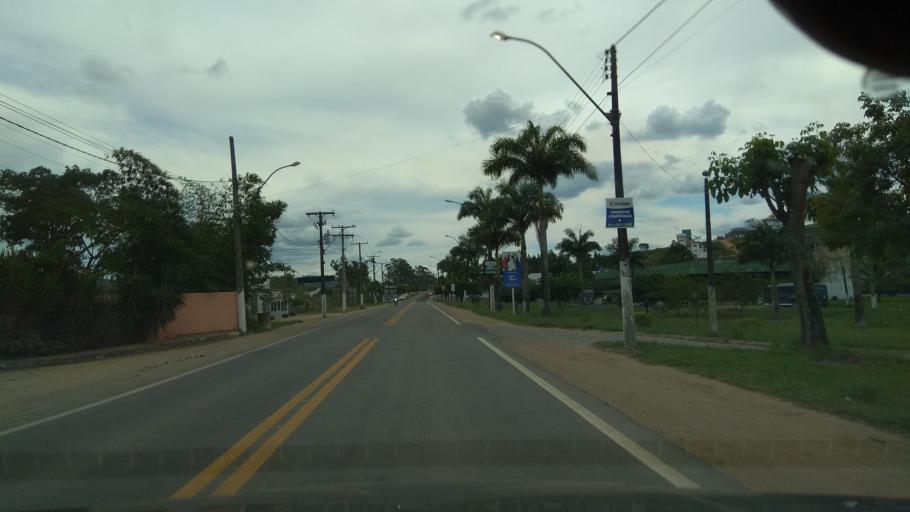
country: BR
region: Bahia
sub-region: Ipiau
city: Ipiau
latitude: -14.1420
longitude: -39.7234
